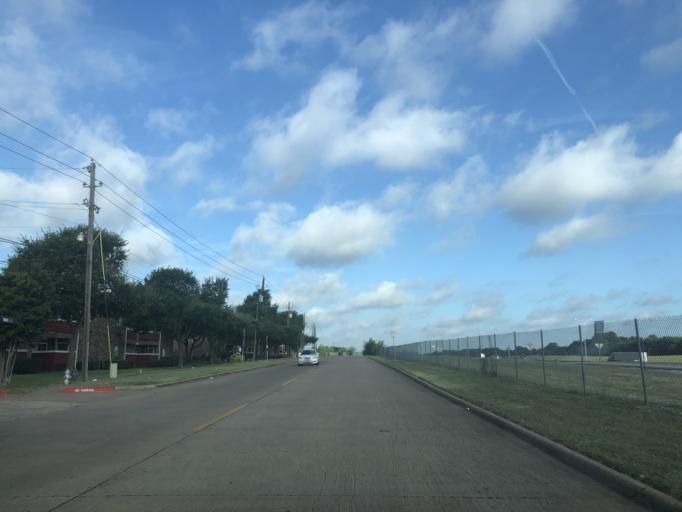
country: US
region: Texas
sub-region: Dallas County
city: Duncanville
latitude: 32.6646
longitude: -96.9096
